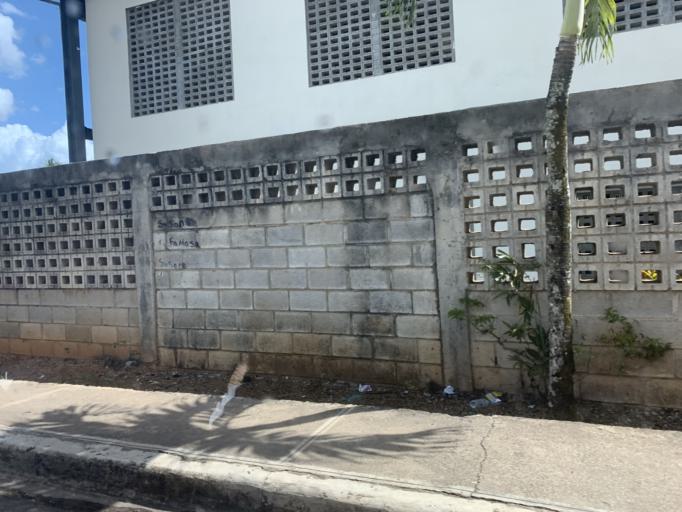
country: DO
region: Monte Plata
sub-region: Yamasa
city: Yamasa
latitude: 18.7712
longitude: -70.0159
